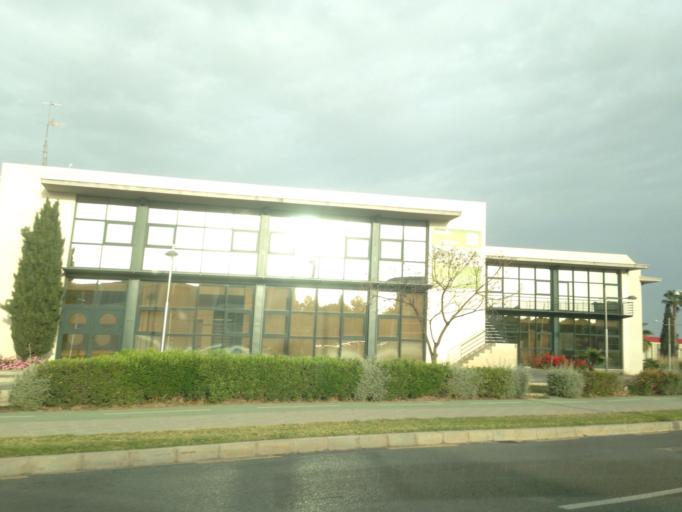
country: ES
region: Andalusia
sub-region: Provincia de Malaga
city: Estacion de Cartama
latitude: 36.7351
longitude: -4.5571
